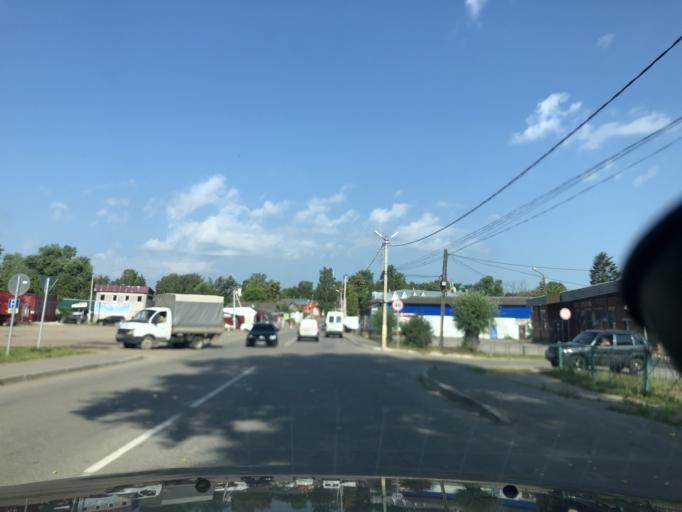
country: RU
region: Tula
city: Dubna
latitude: 54.1506
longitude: 36.9665
